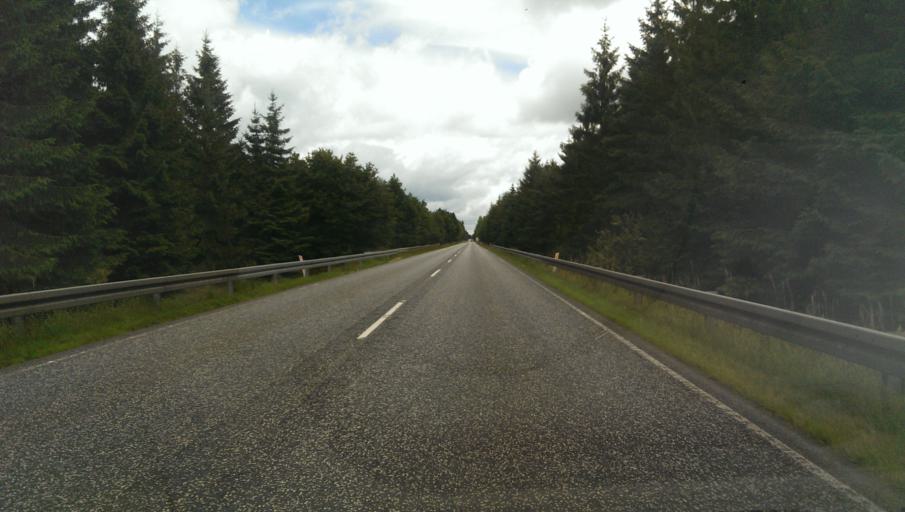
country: DK
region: Central Jutland
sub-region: Ikast-Brande Kommune
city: Bording Kirkeby
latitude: 56.0350
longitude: 9.3771
